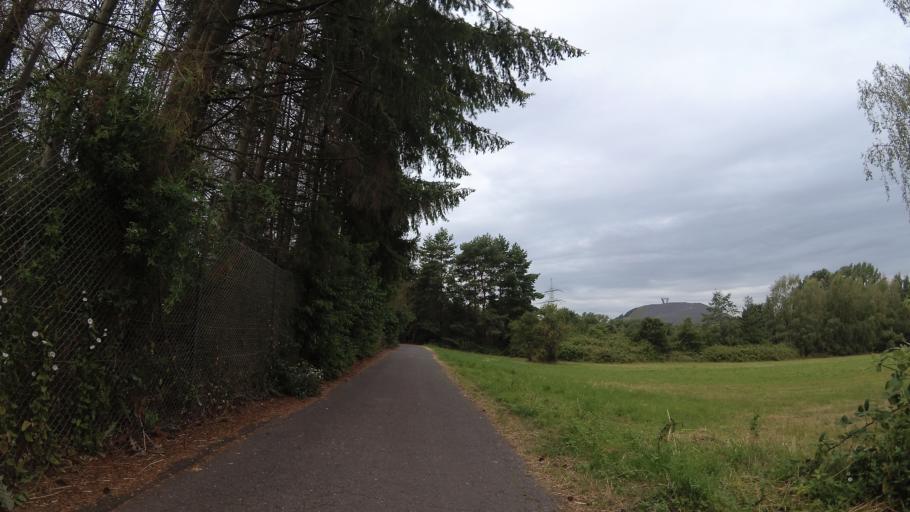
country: DE
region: Saarland
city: Schwalbach
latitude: 49.3114
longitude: 6.8078
